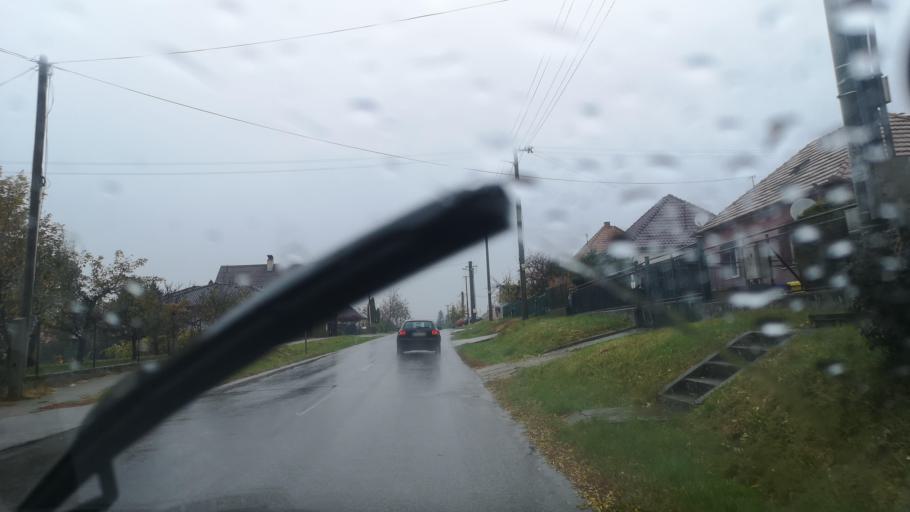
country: SK
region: Nitriansky
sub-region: Okres Nitra
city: Nitra
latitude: 48.2884
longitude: 18.1358
